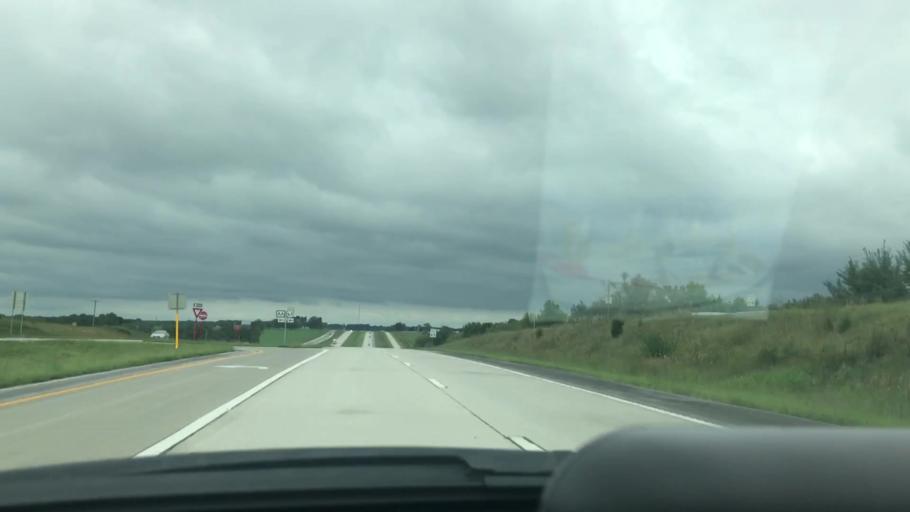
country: US
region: Missouri
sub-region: Greene County
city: Fair Grove
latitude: 37.4257
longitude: -93.1449
